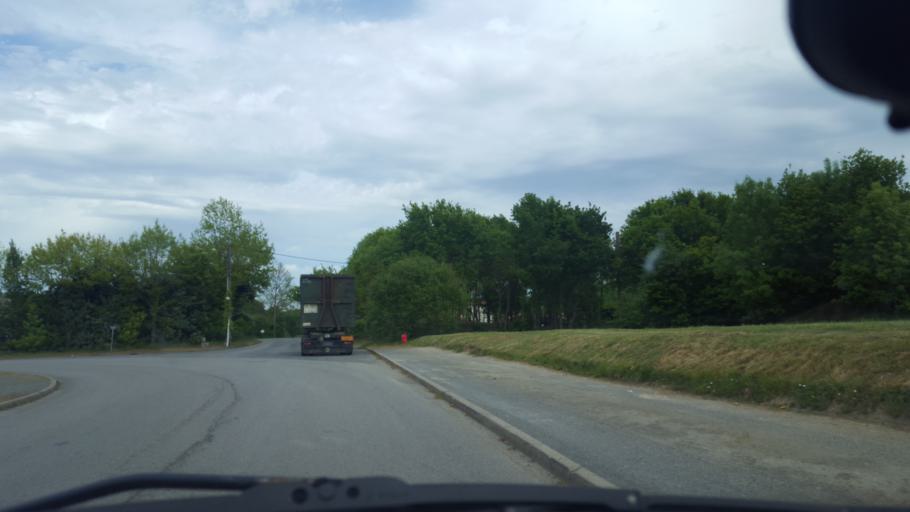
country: FR
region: Pays de la Loire
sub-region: Departement de la Loire-Atlantique
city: Machecoul
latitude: 46.9823
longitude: -1.8040
